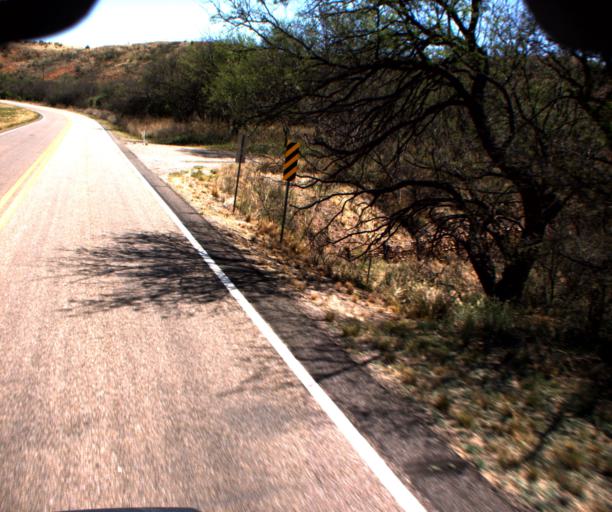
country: US
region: Arizona
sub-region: Santa Cruz County
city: Rio Rico
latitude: 31.5261
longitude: -110.7696
